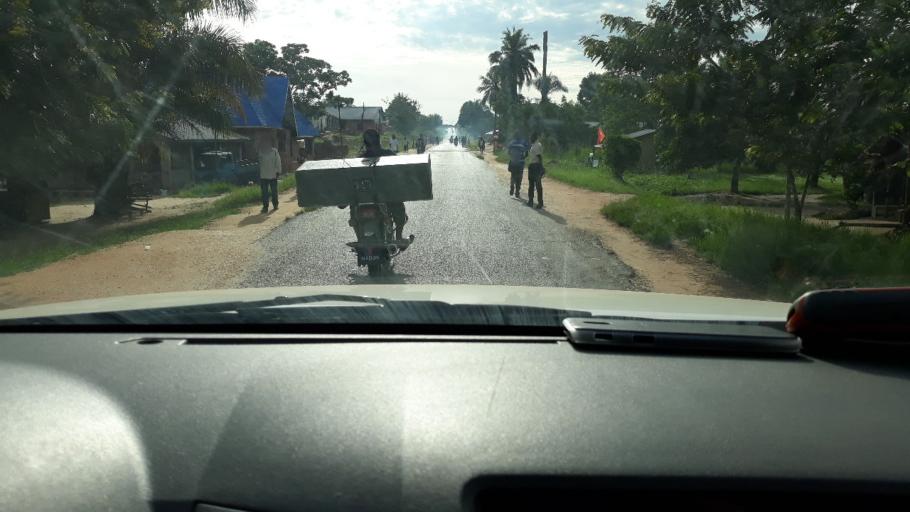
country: CD
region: Maniema
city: Kindu
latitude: -2.9519
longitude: 25.9429
